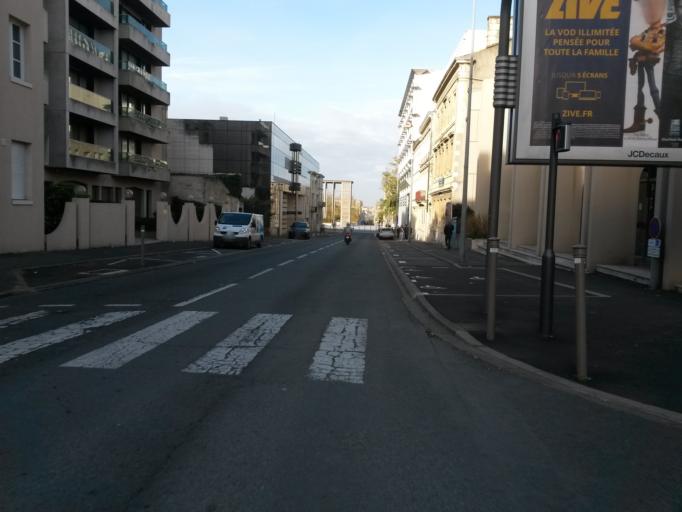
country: FR
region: Poitou-Charentes
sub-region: Departement des Deux-Sevres
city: Niort
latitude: 46.3217
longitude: -0.4554
